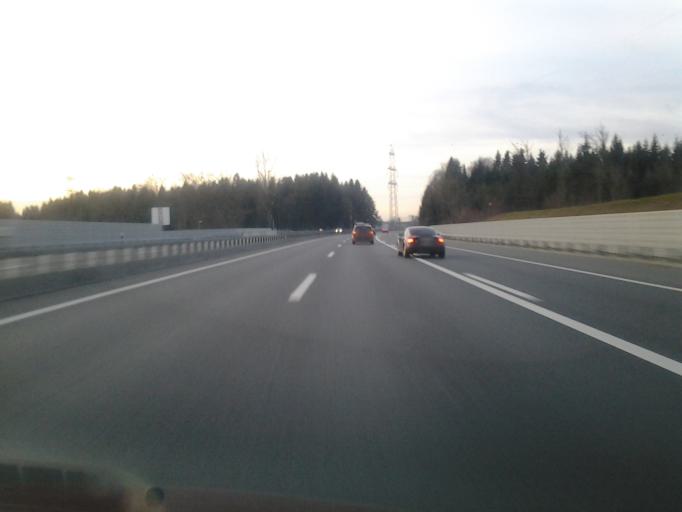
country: CH
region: Lucerne
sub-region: Hochdorf District
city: Emmen
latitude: 47.0903
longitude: 8.2500
